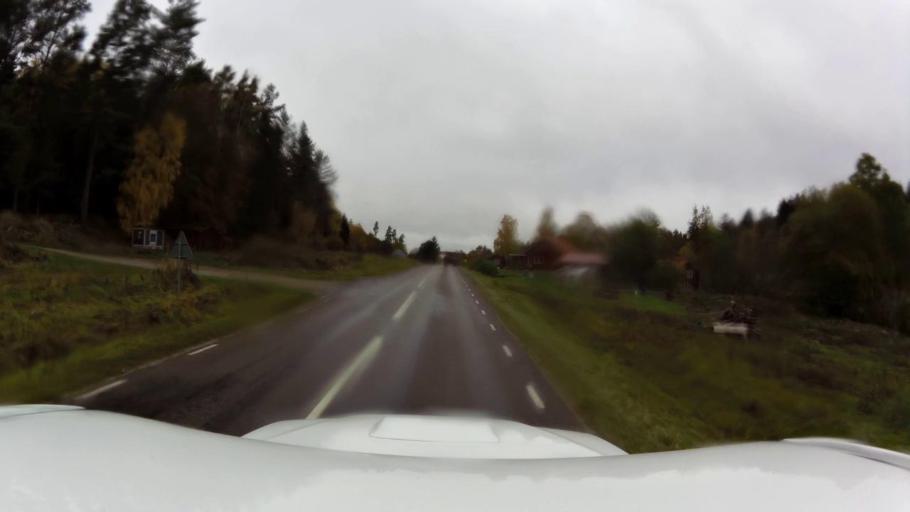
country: SE
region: OEstergoetland
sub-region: Linkopings Kommun
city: Linghem
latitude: 58.4388
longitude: 15.8917
